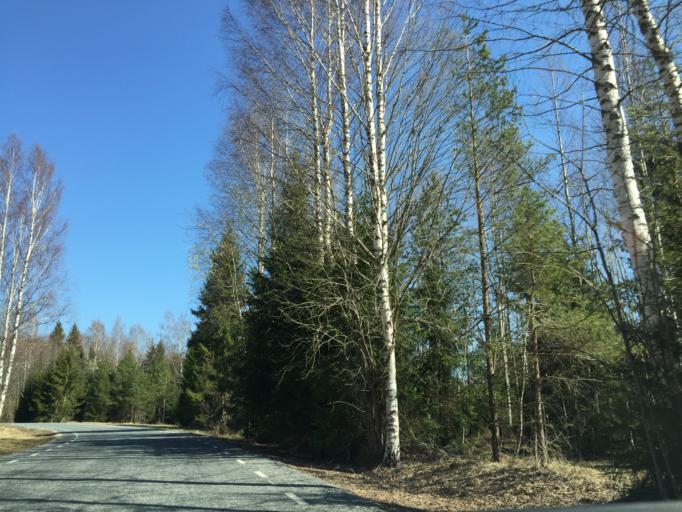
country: EE
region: Tartu
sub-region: Alatskivi vald
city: Kallaste
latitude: 58.5909
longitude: 27.0640
